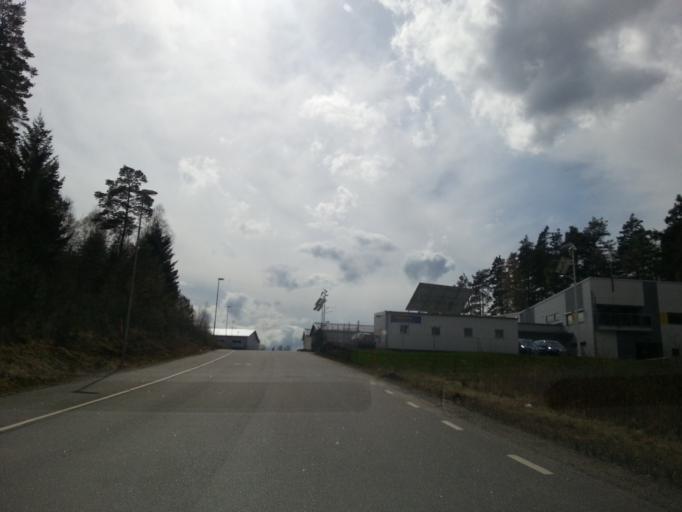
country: SE
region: Vaestra Goetaland
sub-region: Kungalvs Kommun
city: Kungalv
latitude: 57.8835
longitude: 11.9373
